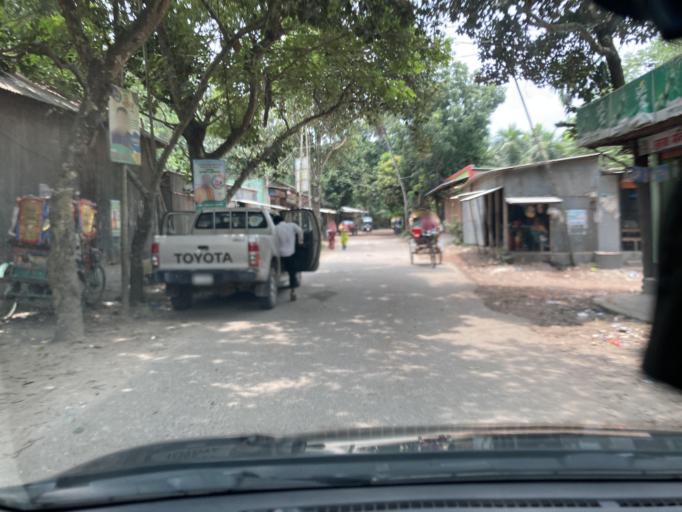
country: BD
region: Dhaka
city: Dohar
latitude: 23.8159
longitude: 90.0468
